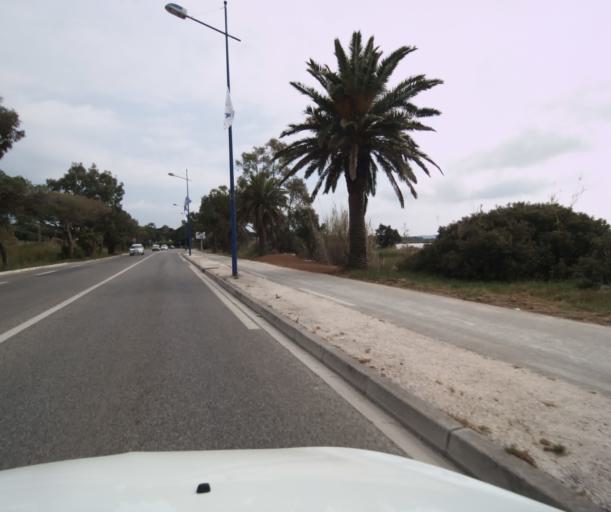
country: FR
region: Provence-Alpes-Cote d'Azur
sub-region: Departement du Var
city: Hyeres
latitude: 43.0844
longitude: 6.1486
